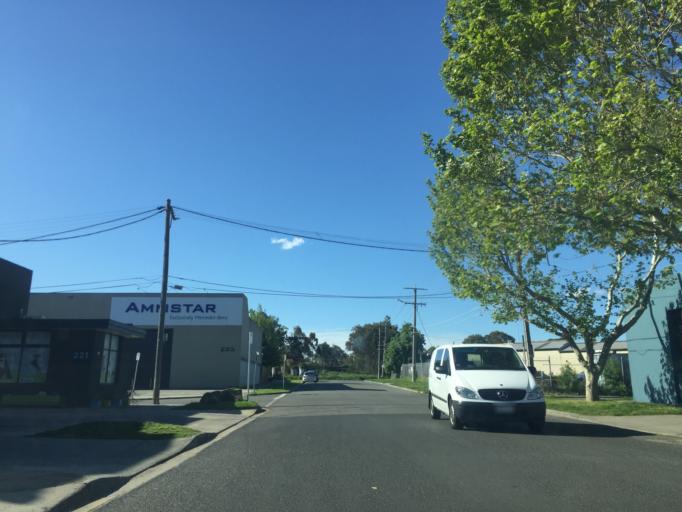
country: AU
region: Victoria
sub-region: Banyule
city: Bellfield
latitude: -37.7657
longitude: 145.0275
